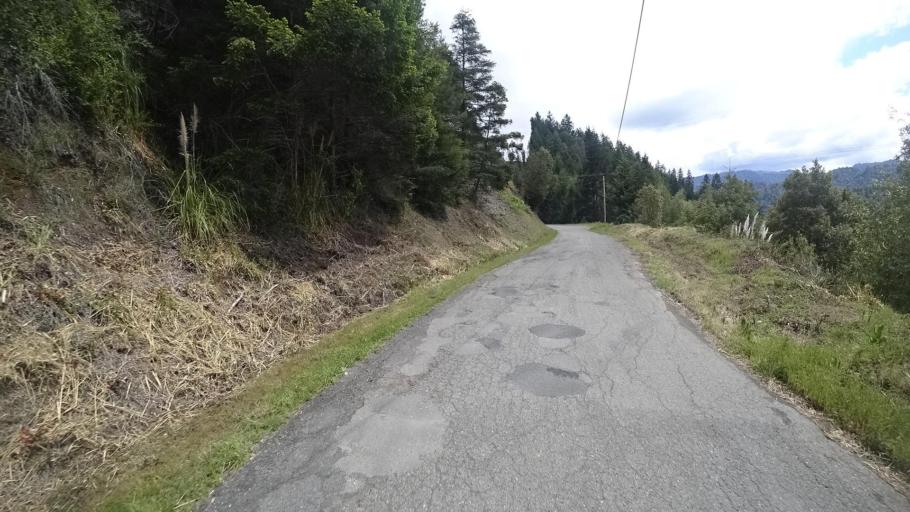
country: US
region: California
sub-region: Humboldt County
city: Blue Lake
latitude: 40.7673
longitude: -123.9303
